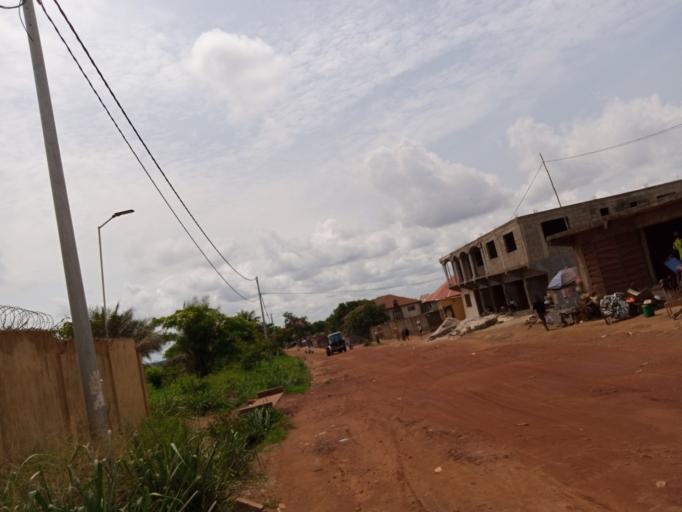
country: SL
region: Western Area
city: Waterloo
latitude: 8.3591
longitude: -13.0797
